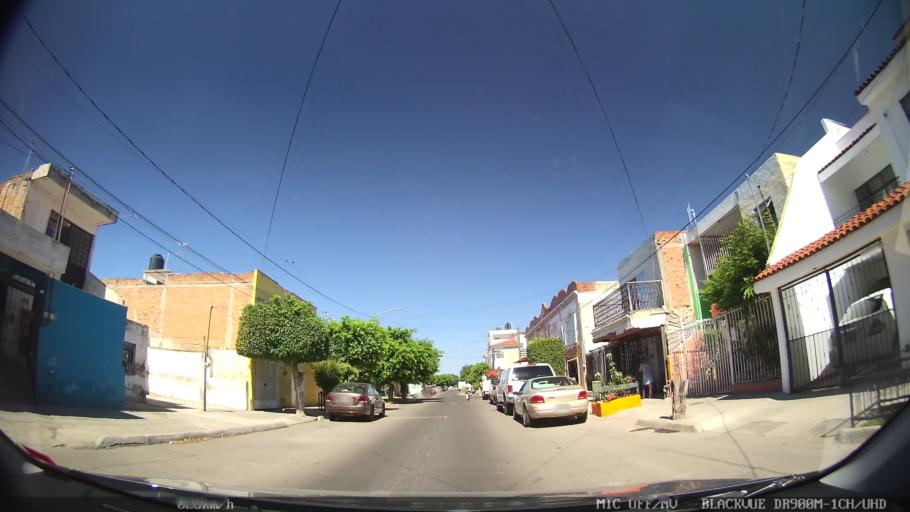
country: MX
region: Jalisco
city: Tlaquepaque
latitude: 20.6565
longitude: -103.2881
